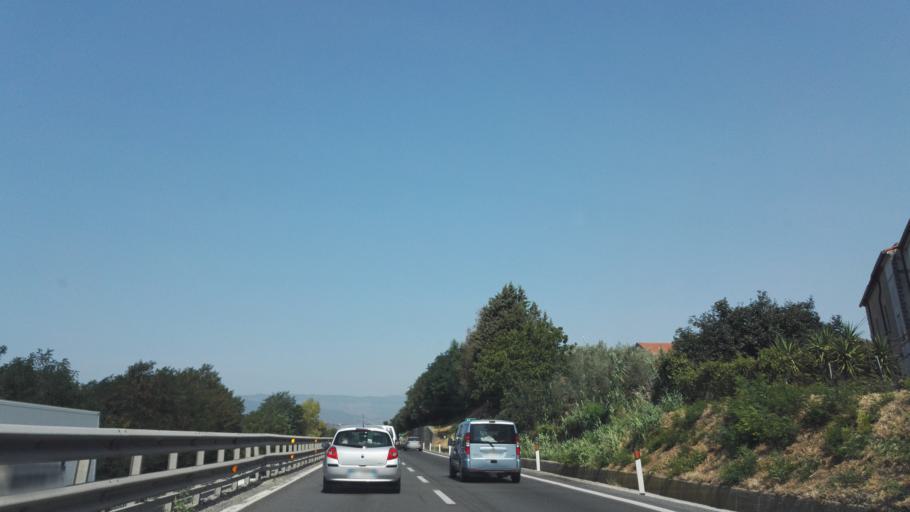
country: IT
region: Calabria
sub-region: Provincia di Cosenza
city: Donnici Inferiore
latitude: 39.2319
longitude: 16.3005
